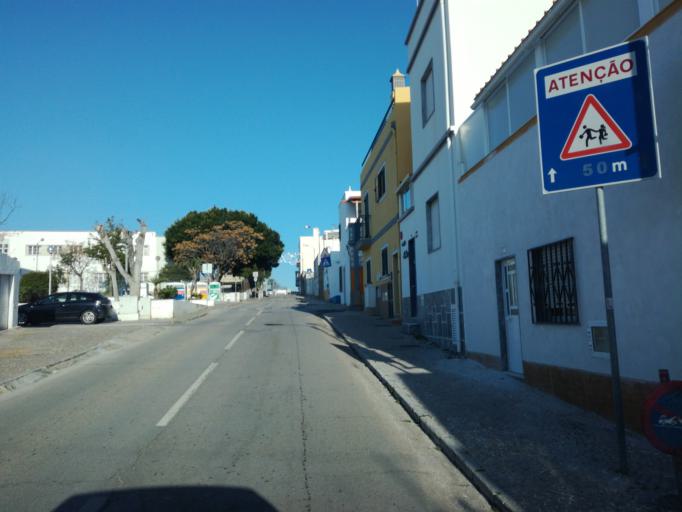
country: PT
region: Faro
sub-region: Olhao
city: Laranjeiro
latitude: 37.0535
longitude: -7.7481
